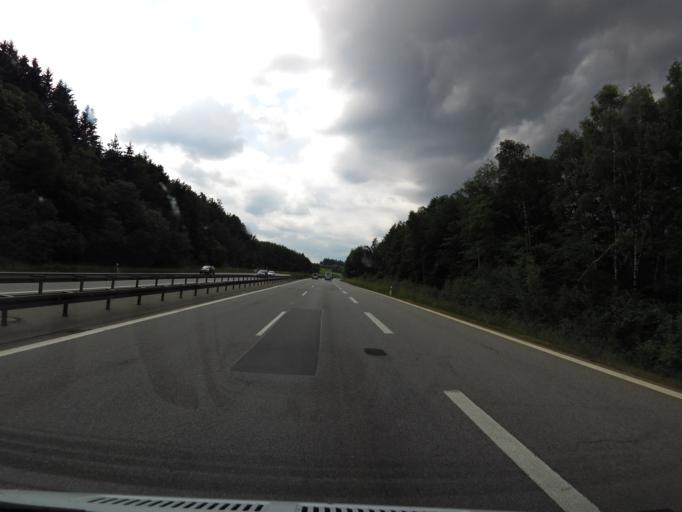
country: DE
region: Bavaria
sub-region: Lower Bavaria
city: Aussernzell
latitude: 48.6871
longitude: 13.2091
